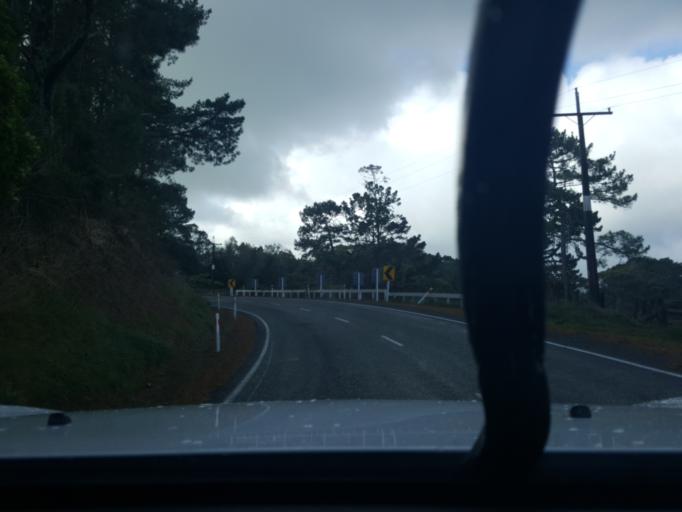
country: NZ
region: Waikato
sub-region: Waikato District
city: Te Kauwhata
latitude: -37.4452
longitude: 175.0819
